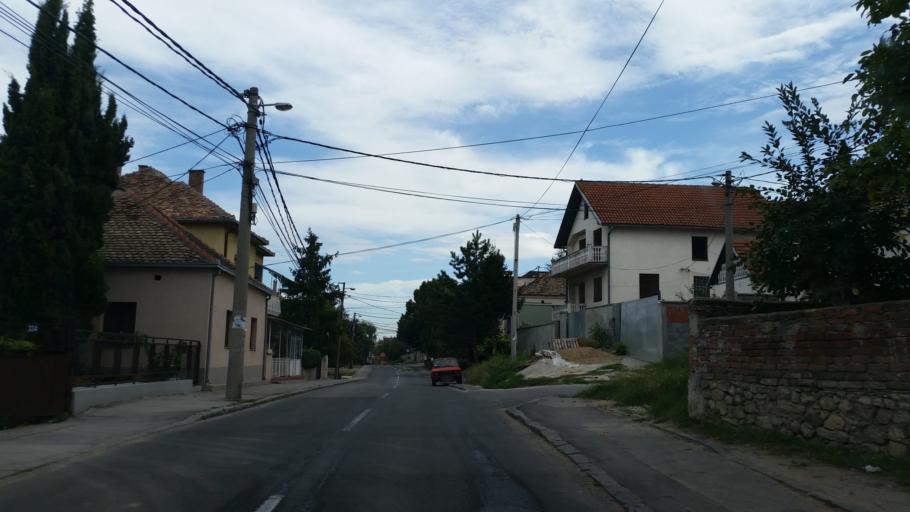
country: RS
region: Central Serbia
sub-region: Belgrade
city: Palilula
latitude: 44.8264
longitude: 20.5431
